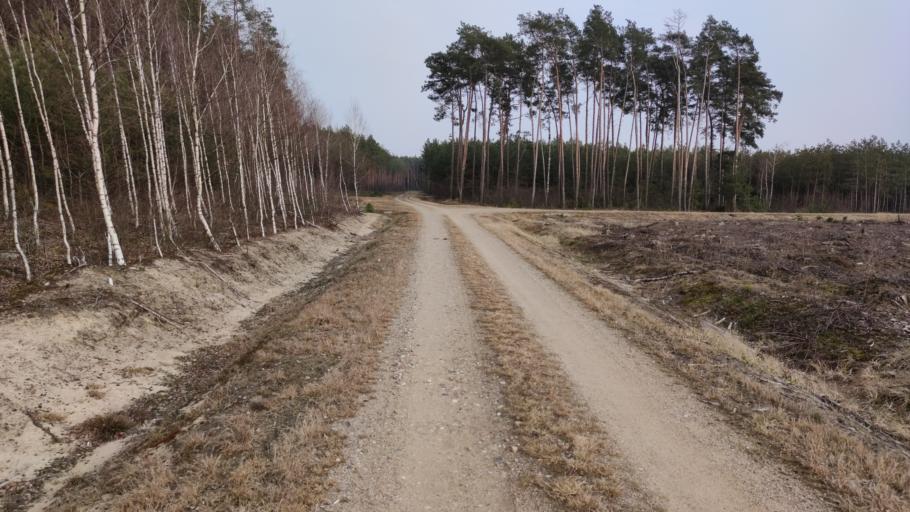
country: PL
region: Masovian Voivodeship
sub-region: Powiat plocki
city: Slubice
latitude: 52.4534
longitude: 19.9563
